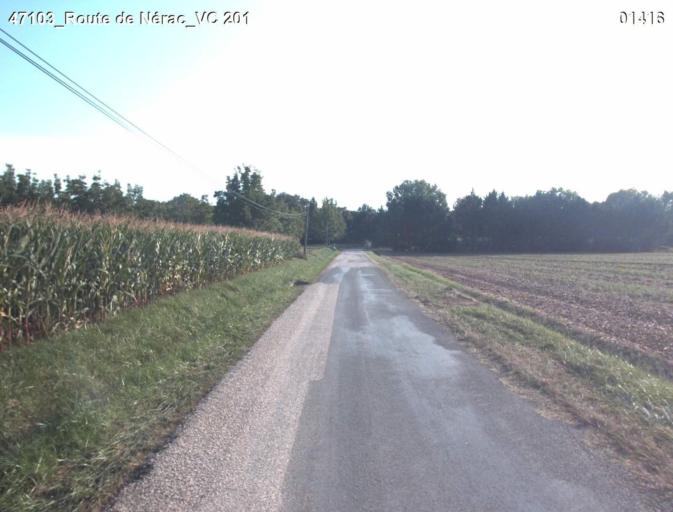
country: FR
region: Aquitaine
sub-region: Departement du Lot-et-Garonne
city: Nerac
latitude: 44.0876
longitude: 0.3329
